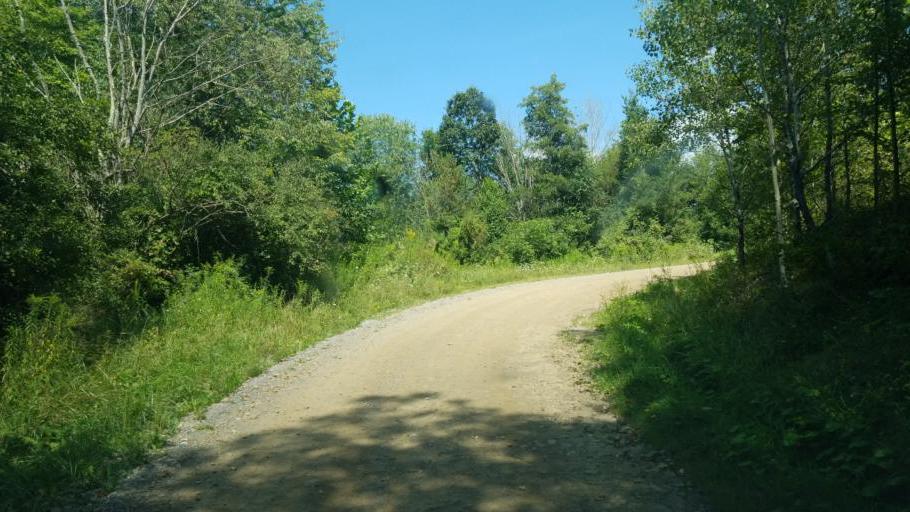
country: US
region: Pennsylvania
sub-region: Clarion County
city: Knox
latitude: 41.1136
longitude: -79.5374
